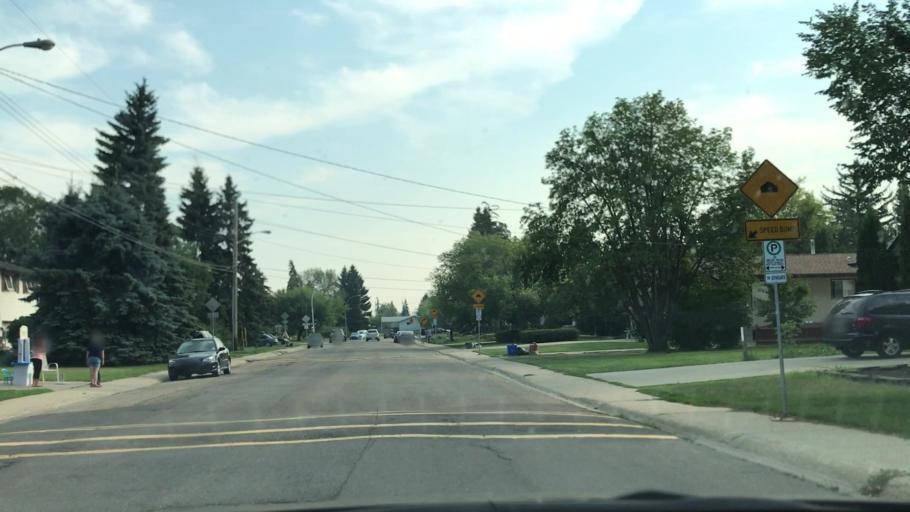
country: CA
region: Alberta
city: Edmonton
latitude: 53.4915
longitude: -113.5119
